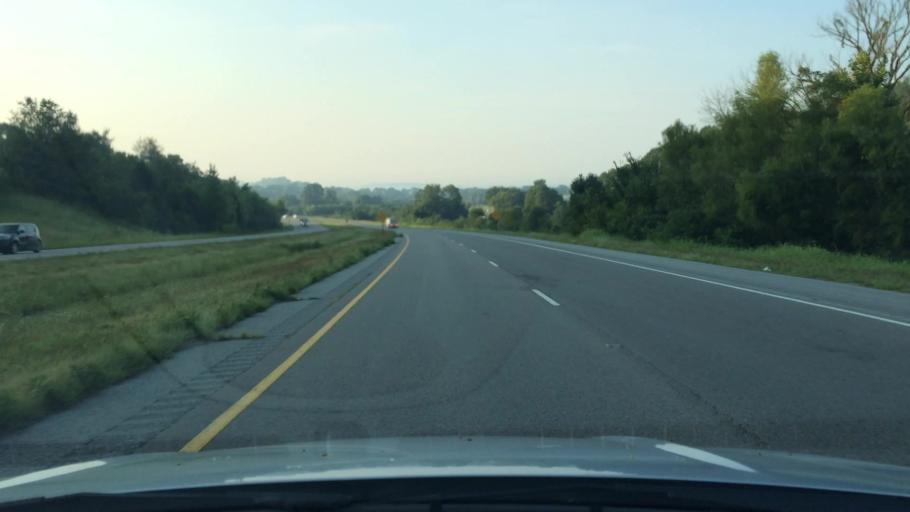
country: US
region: Tennessee
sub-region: Giles County
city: Pulaski
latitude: 35.1752
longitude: -87.0590
